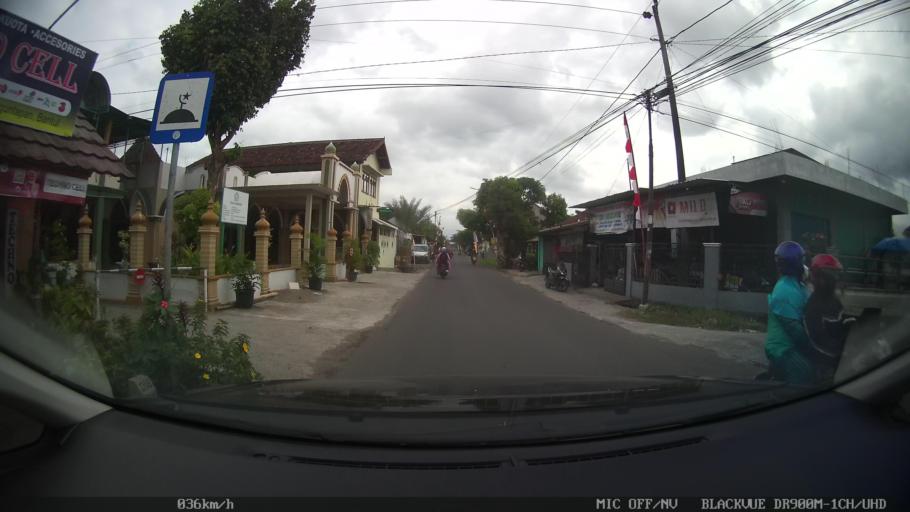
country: ID
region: Daerah Istimewa Yogyakarta
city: Depok
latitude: -7.8311
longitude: 110.4230
